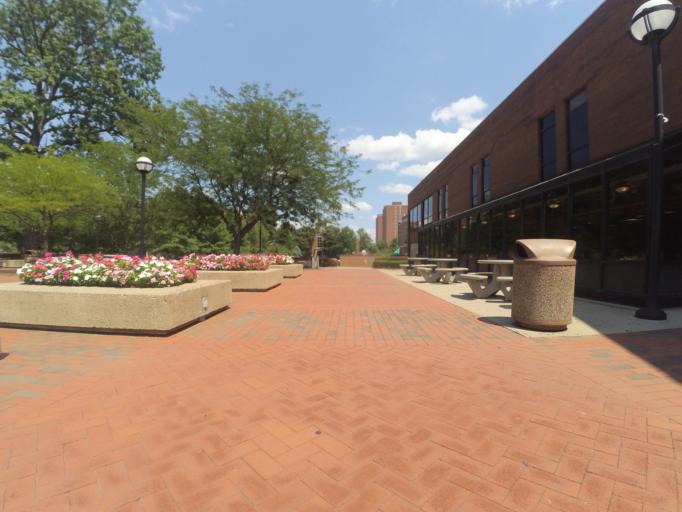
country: US
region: West Virginia
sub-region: Cabell County
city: Huntington
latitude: 38.4227
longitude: -82.4290
